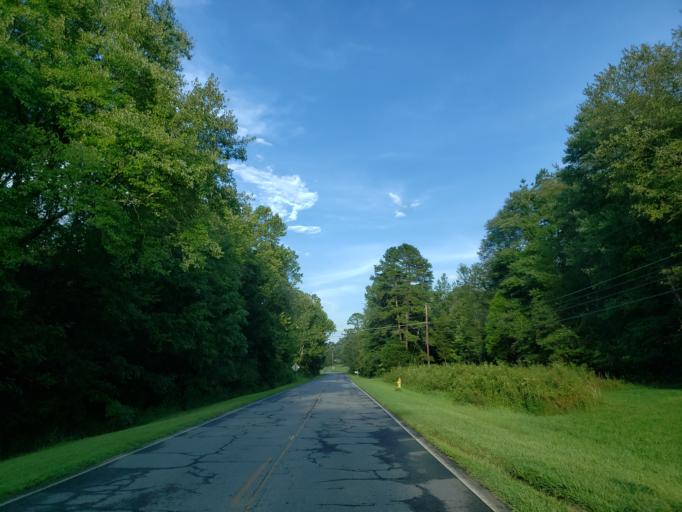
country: US
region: Georgia
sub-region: Bartow County
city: Euharlee
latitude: 34.2282
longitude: -84.9643
